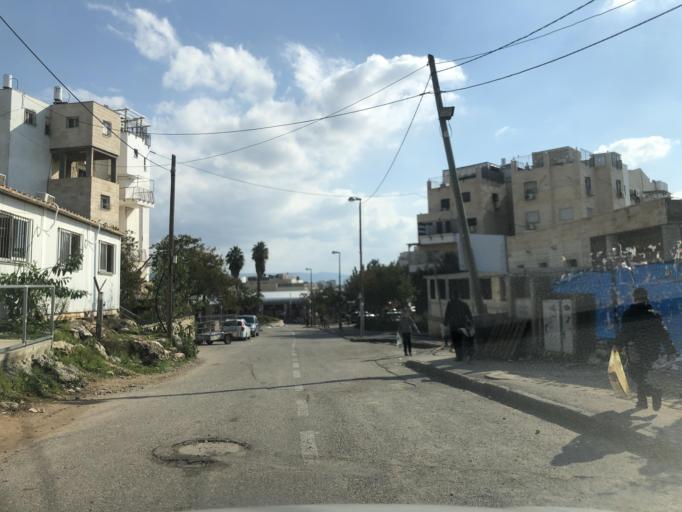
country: IL
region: Jerusalem
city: Modiin Ilit
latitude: 31.9403
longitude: 35.0378
